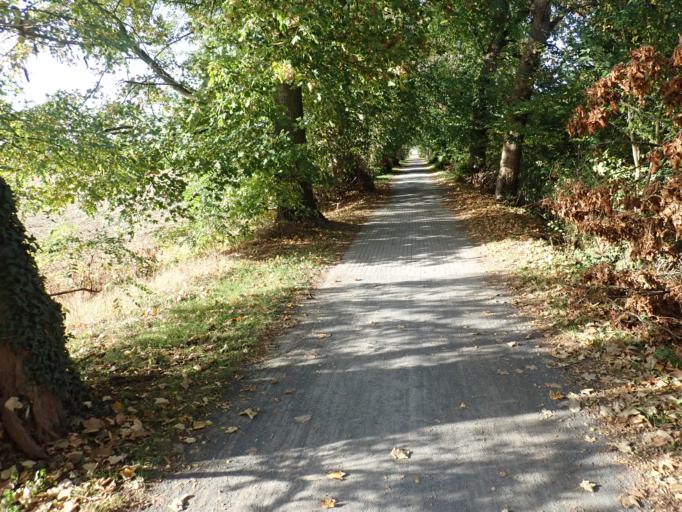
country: BE
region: Flanders
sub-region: Provincie Vlaams-Brabant
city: Rotselaar
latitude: 50.9447
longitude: 4.7356
